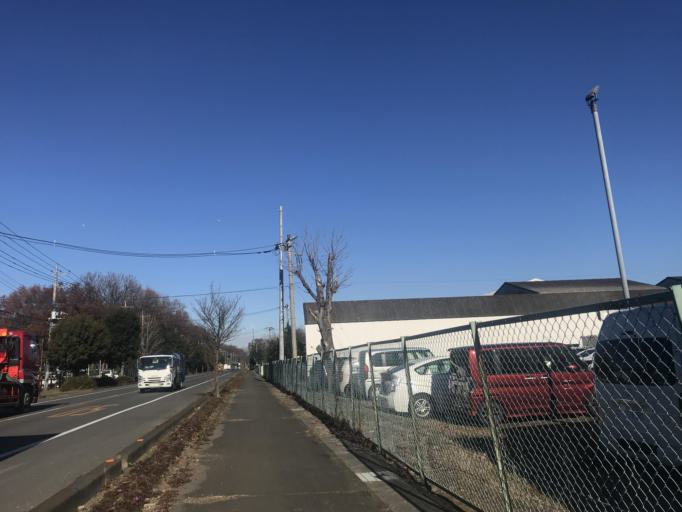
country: JP
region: Ibaraki
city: Yuki
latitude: 36.3319
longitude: 139.8798
